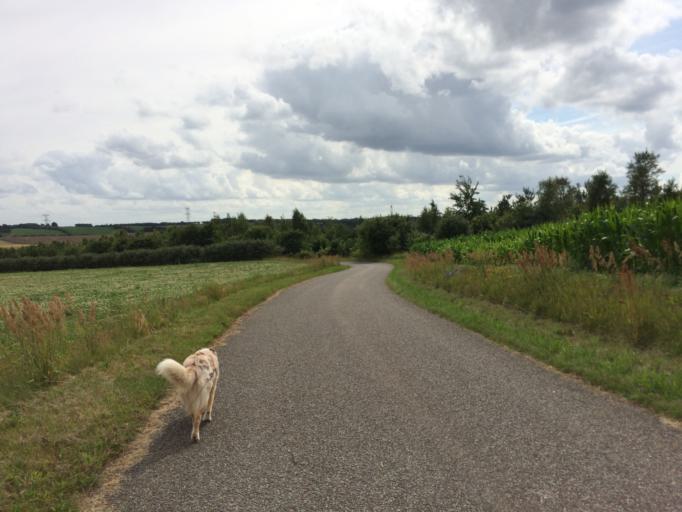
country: DK
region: Central Jutland
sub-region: Viborg Kommune
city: Viborg
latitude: 56.4958
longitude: 9.5310
